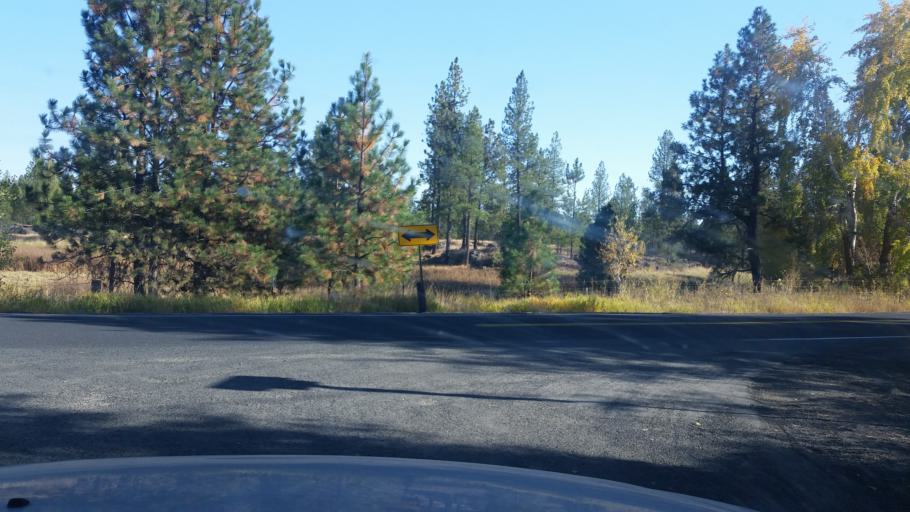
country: US
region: Washington
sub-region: Spokane County
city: Cheney
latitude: 47.4158
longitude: -117.6476
